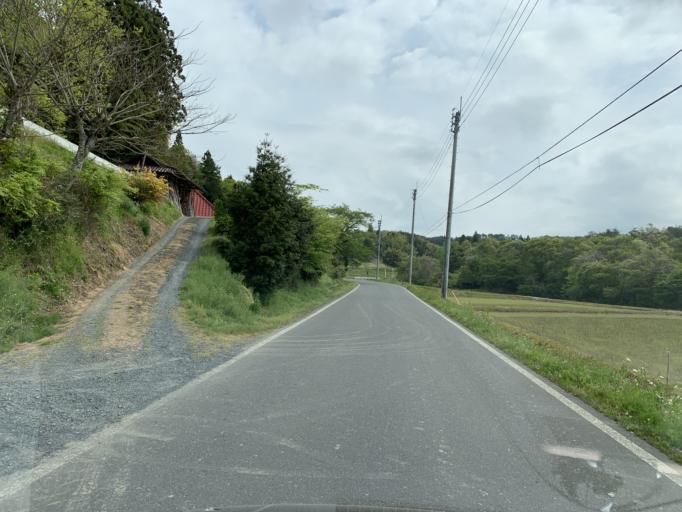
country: JP
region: Iwate
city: Ichinoseki
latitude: 38.8443
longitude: 141.1940
